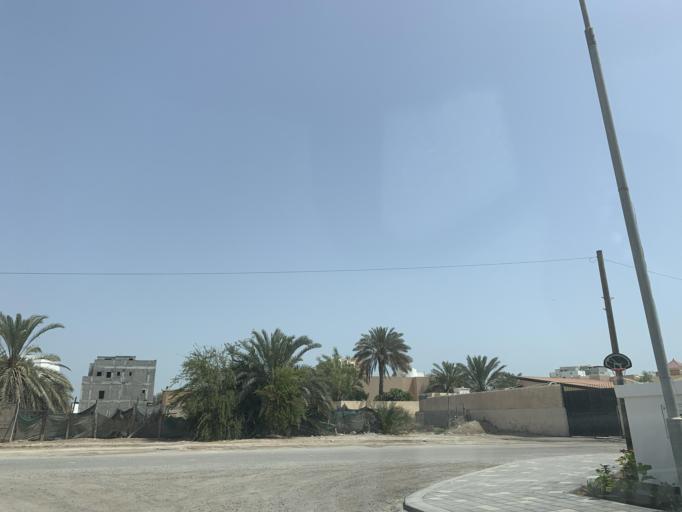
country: BH
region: Northern
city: Sitrah
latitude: 26.1574
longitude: 50.5878
